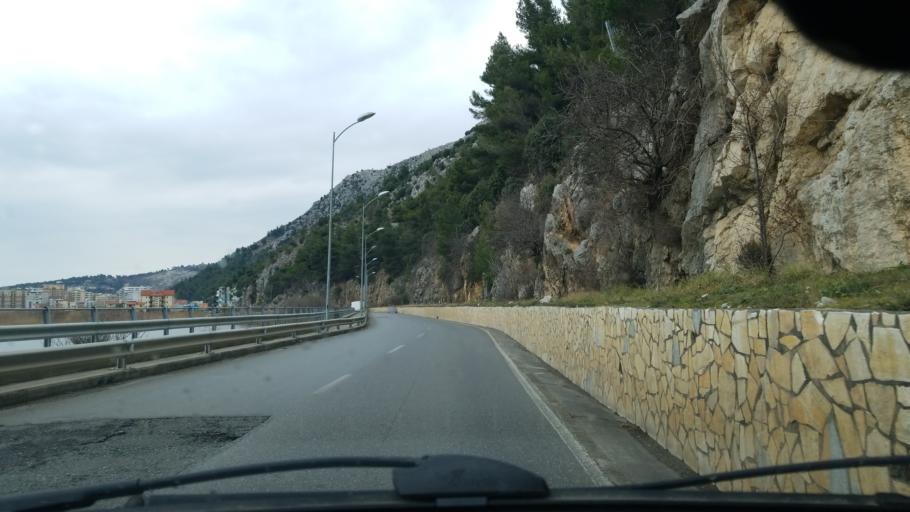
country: AL
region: Lezhe
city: Shengjin
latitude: 41.8041
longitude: 19.6137
